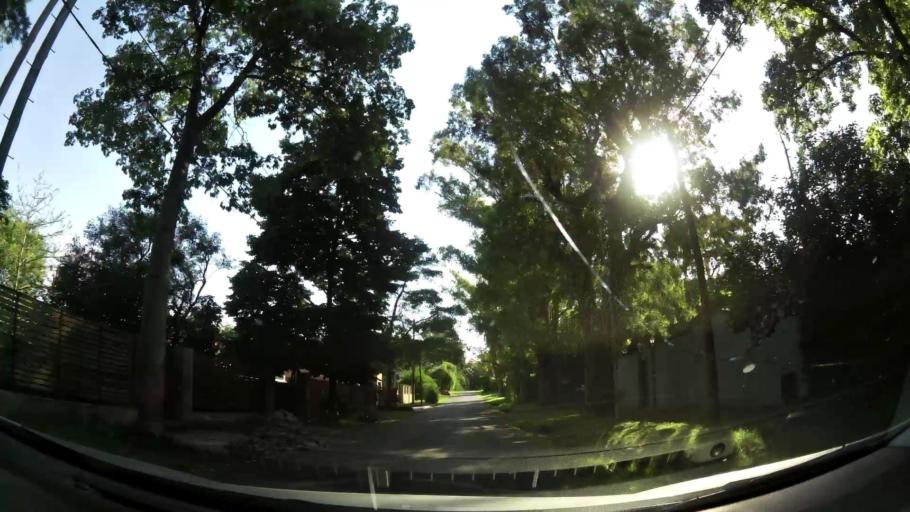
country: AR
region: Buenos Aires
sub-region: Partido de Tigre
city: Tigre
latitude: -34.4702
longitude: -58.6310
